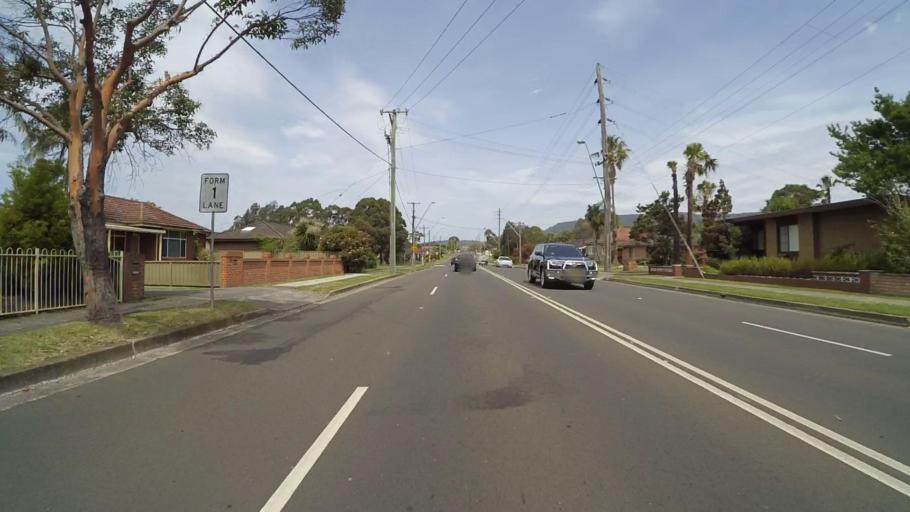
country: AU
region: New South Wales
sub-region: Shellharbour
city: Albion Park Rail
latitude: -34.5745
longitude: 150.7761
